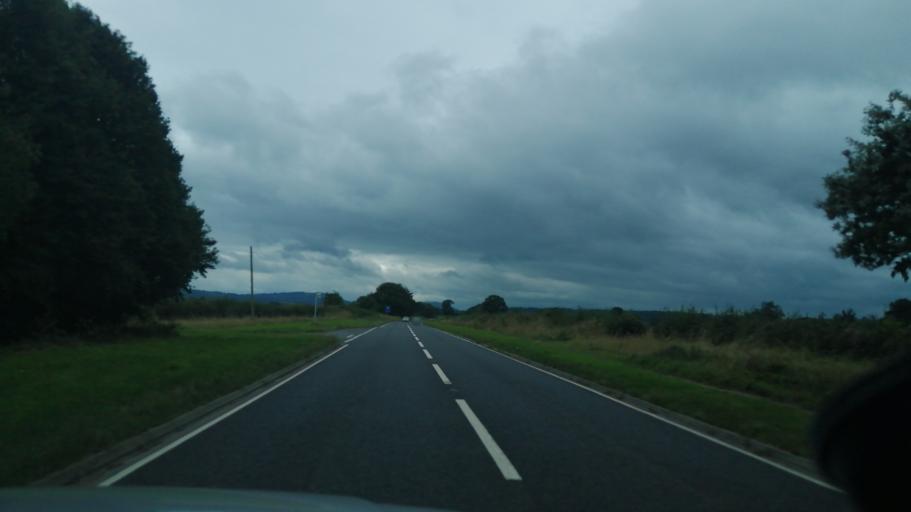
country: GB
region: England
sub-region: Herefordshire
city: Thruxton
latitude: 52.0131
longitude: -2.7875
